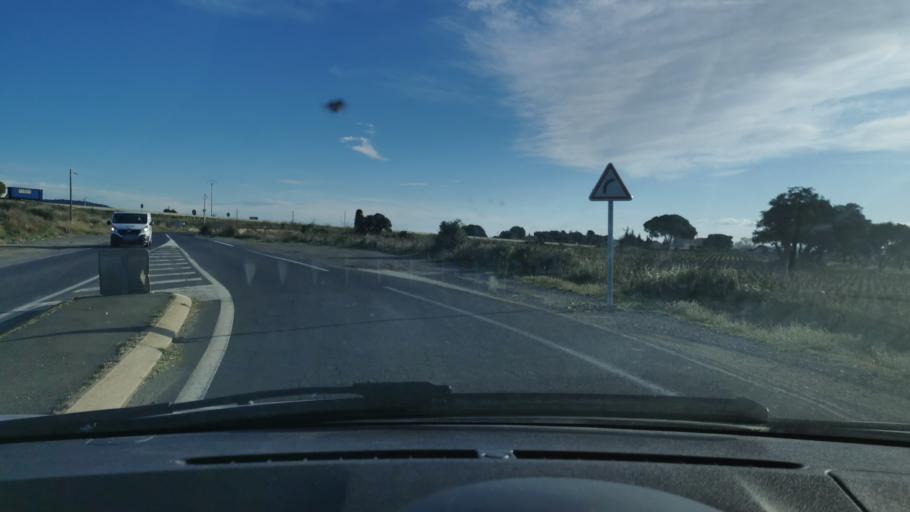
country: FR
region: Languedoc-Roussillon
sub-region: Departement de l'Herault
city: Balaruc-le-Vieux
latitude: 43.4447
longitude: 3.7099
